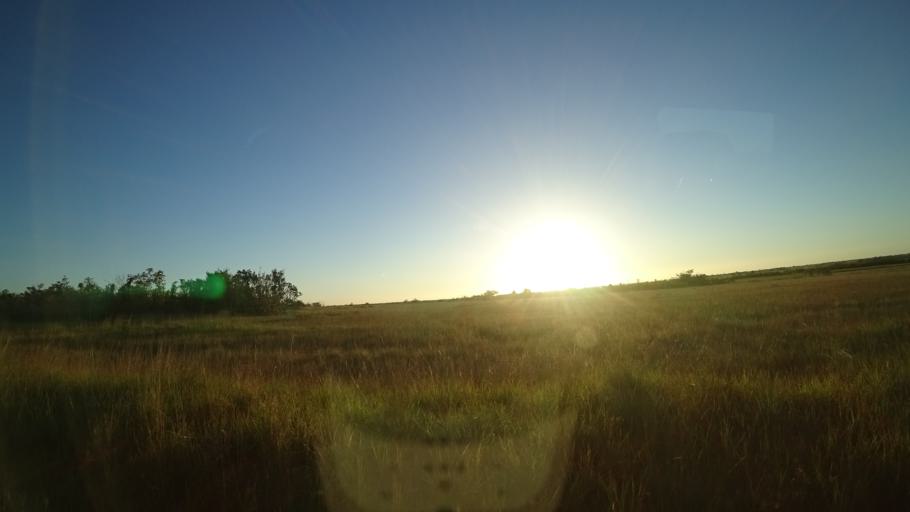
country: MZ
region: Sofala
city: Beira
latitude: -19.6334
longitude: 35.0597
